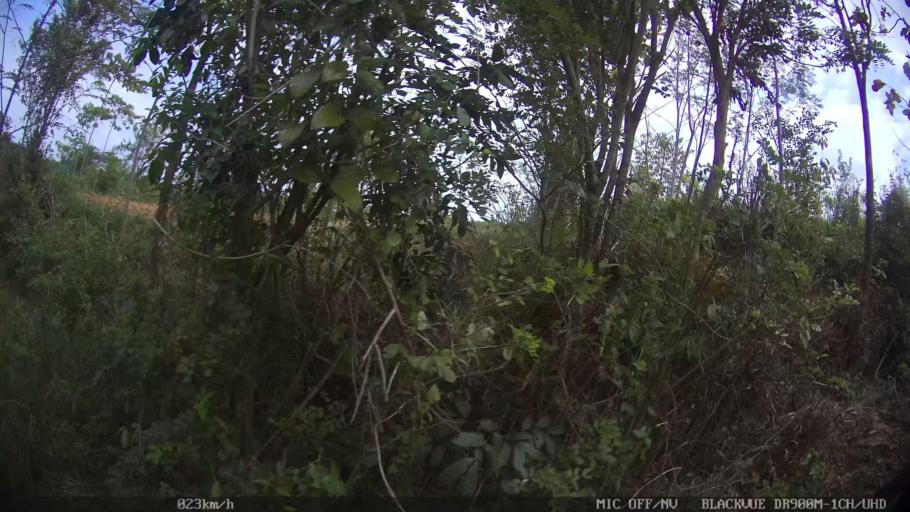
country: ID
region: Central Java
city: Candi Prambanan
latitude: -7.8155
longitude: 110.5249
